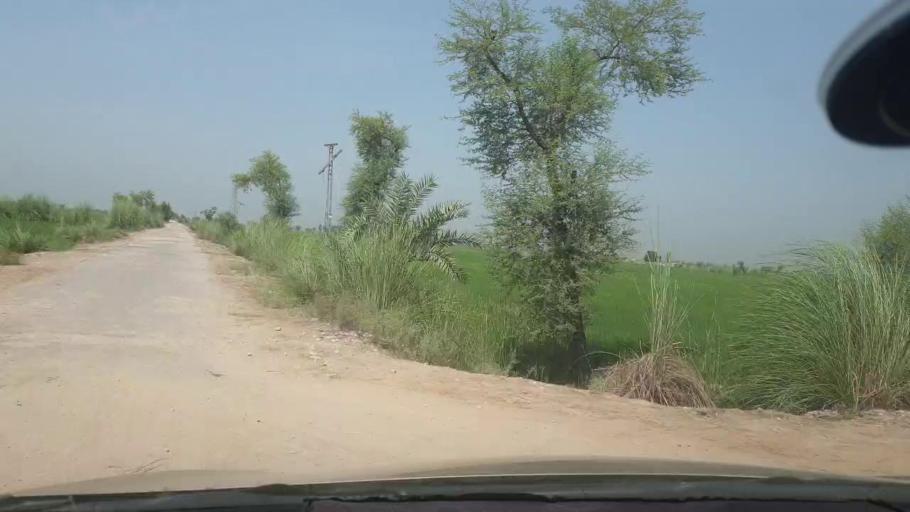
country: PK
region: Sindh
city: Shahdadkot
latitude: 27.7569
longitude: 67.9536
